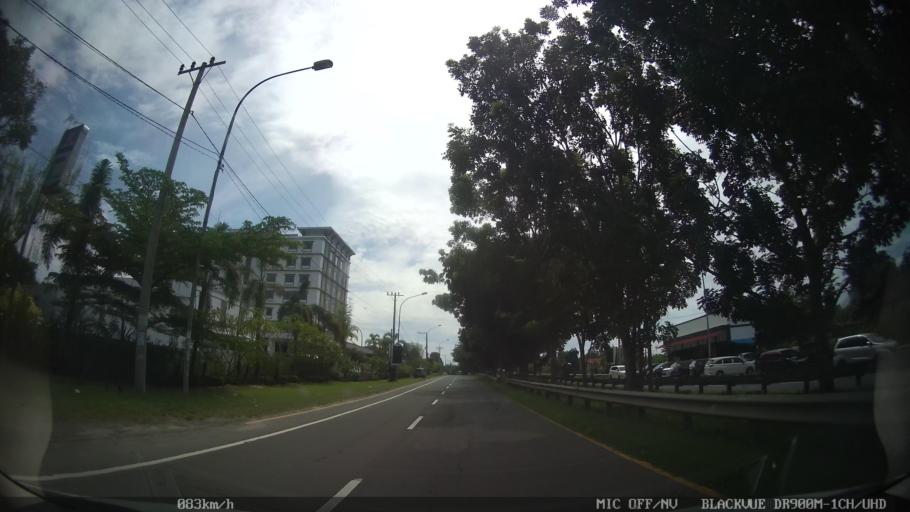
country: ID
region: North Sumatra
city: Percut
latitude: 3.5990
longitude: 98.8318
